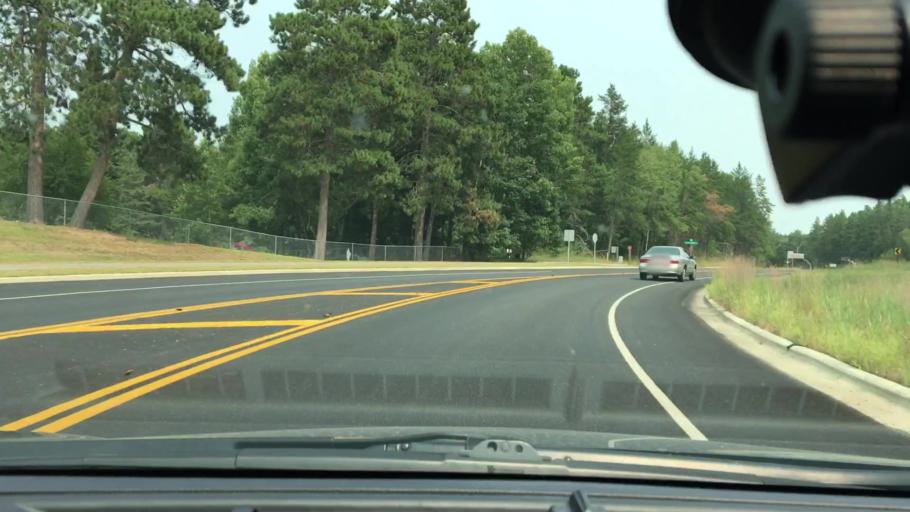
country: US
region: Minnesota
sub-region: Crow Wing County
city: Nisswa
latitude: 46.5213
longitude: -94.2798
